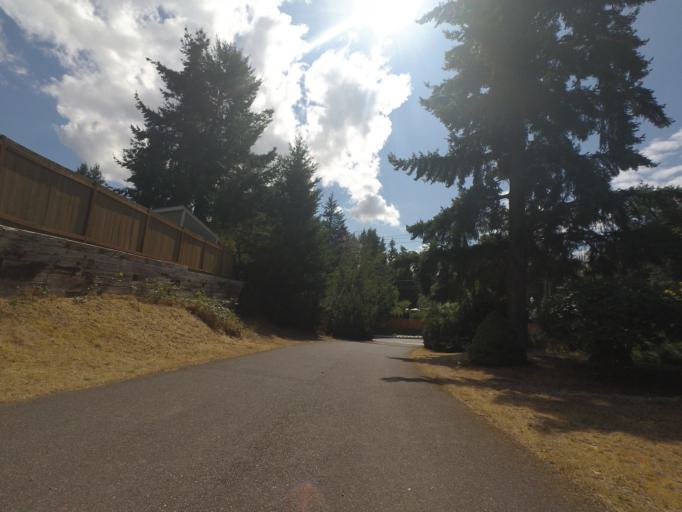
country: US
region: Washington
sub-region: Pierce County
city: Fircrest
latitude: 47.2095
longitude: -122.5213
